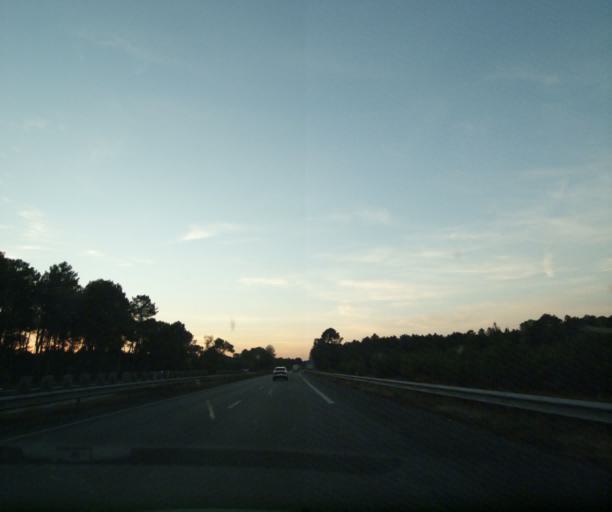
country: FR
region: Aquitaine
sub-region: Departement de la Gironde
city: Illats
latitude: 44.6355
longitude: -0.4199
